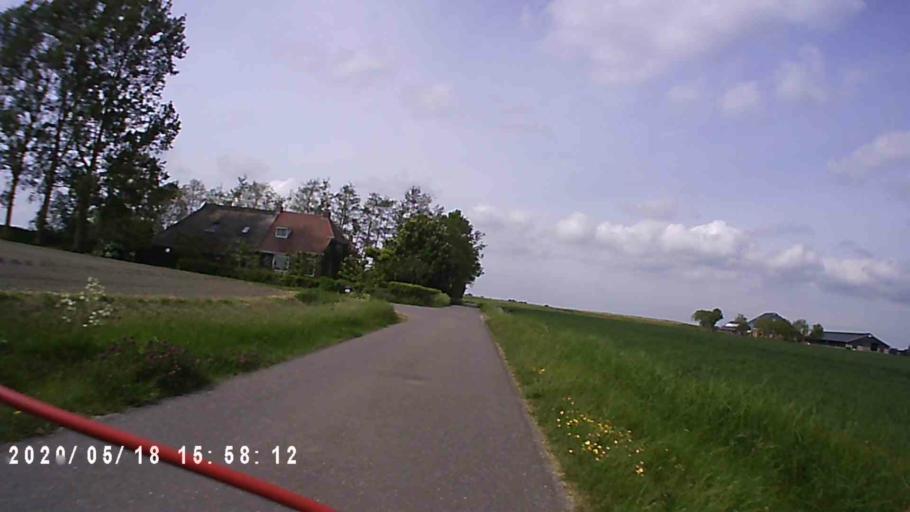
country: NL
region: Groningen
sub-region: Gemeente Zuidhorn
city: Oldehove
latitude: 53.3139
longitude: 6.4408
